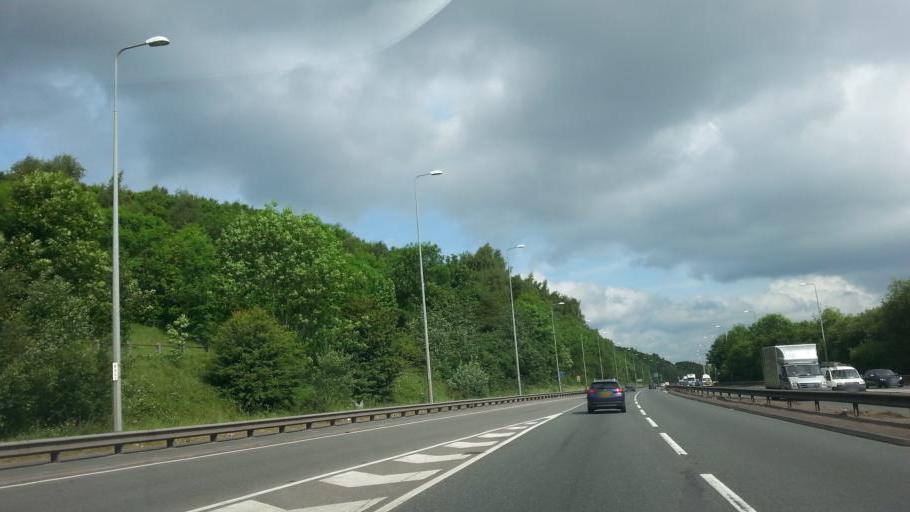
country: GB
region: England
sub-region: Stoke-on-Trent
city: Stoke-on-Trent
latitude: 53.0214
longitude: -2.2058
